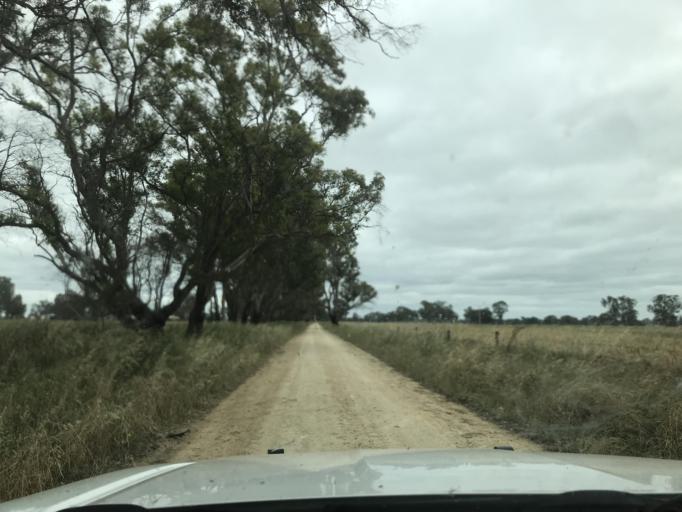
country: AU
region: South Australia
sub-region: Wattle Range
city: Penola
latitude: -37.1800
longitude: 141.0690
